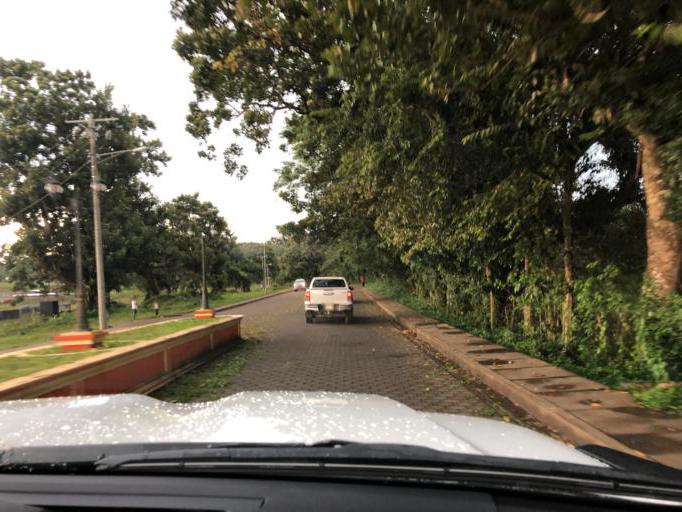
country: NI
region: Chontales
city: La Libertad
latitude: 12.2099
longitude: -85.1688
